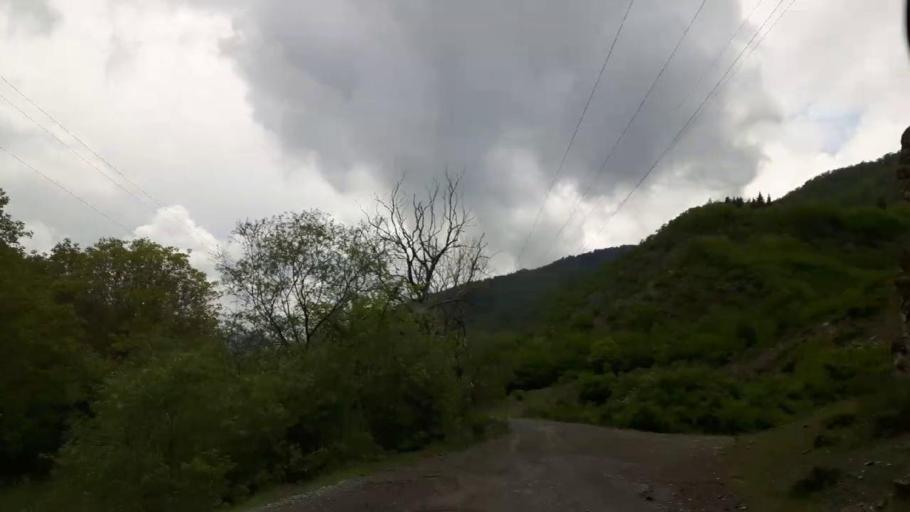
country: GE
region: Shida Kartli
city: Gori
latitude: 41.8833
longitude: 43.9977
